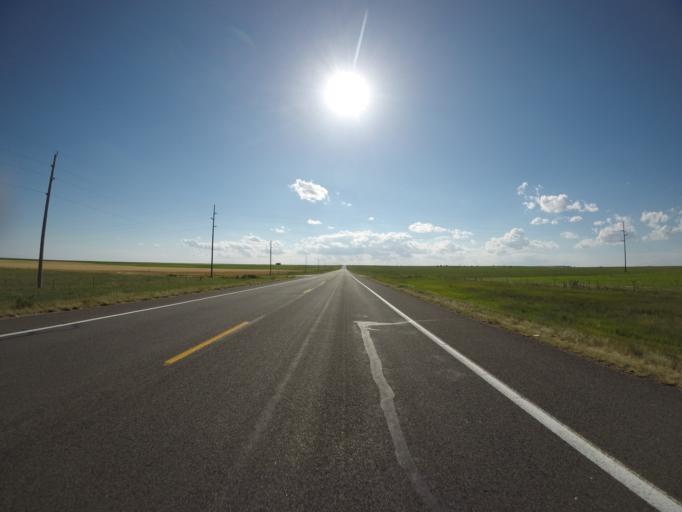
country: US
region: Colorado
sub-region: Morgan County
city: Fort Morgan
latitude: 40.6107
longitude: -103.7524
